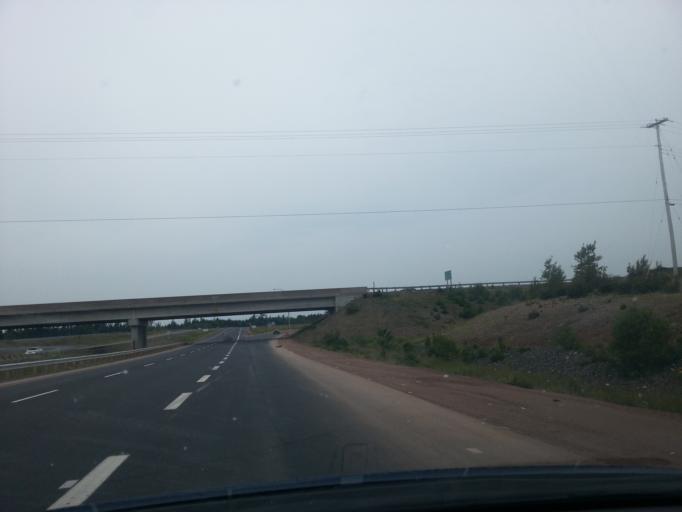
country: CA
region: Nova Scotia
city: Truro
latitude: 45.4095
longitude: -63.5305
